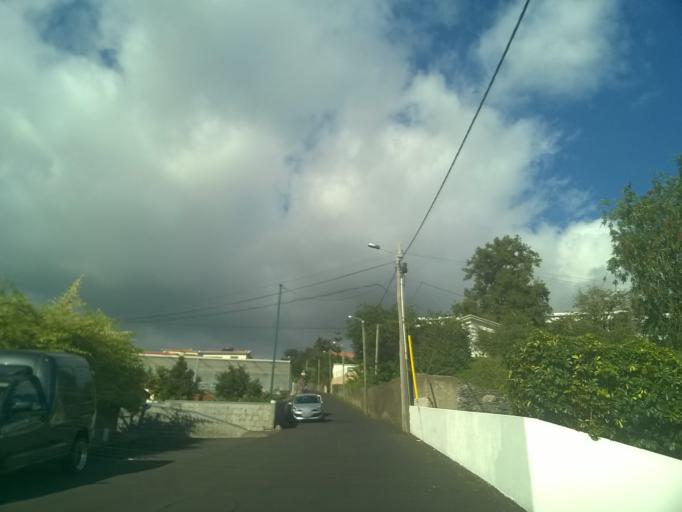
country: PT
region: Madeira
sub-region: Funchal
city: Nossa Senhora do Monte
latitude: 32.6677
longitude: -16.9058
